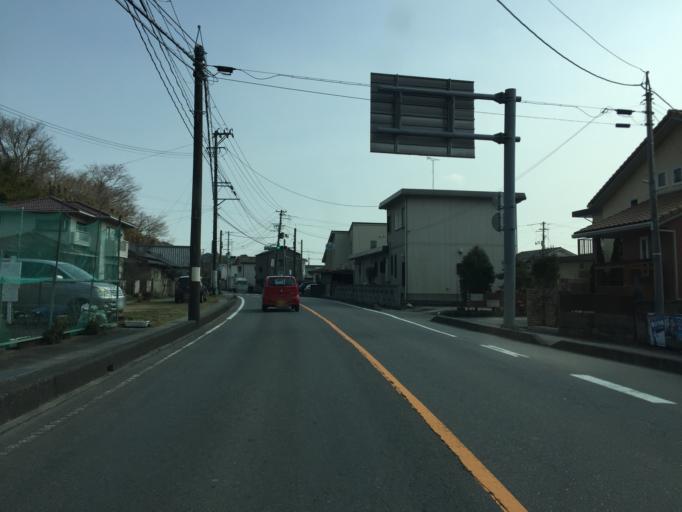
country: JP
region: Ibaraki
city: Kitaibaraki
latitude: 36.9202
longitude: 140.7878
